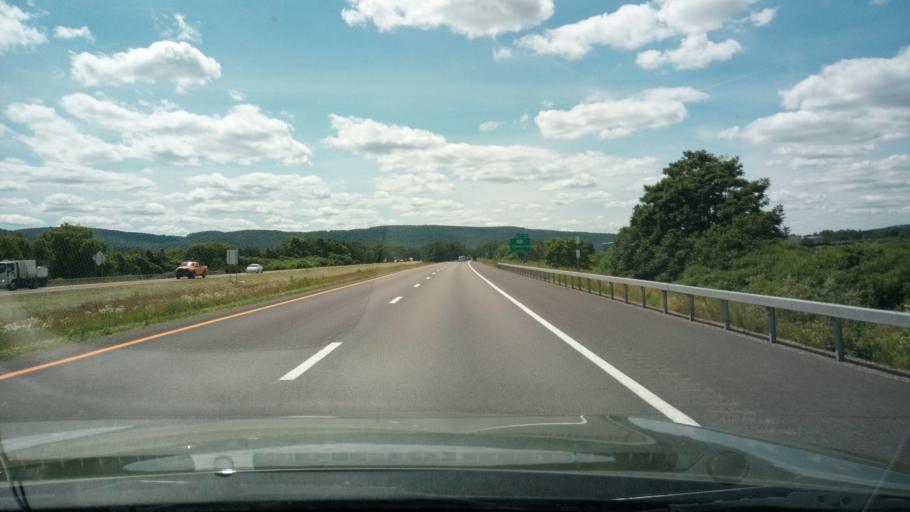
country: US
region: Pennsylvania
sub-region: Bradford County
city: South Waverly
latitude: 42.0012
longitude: -76.6052
